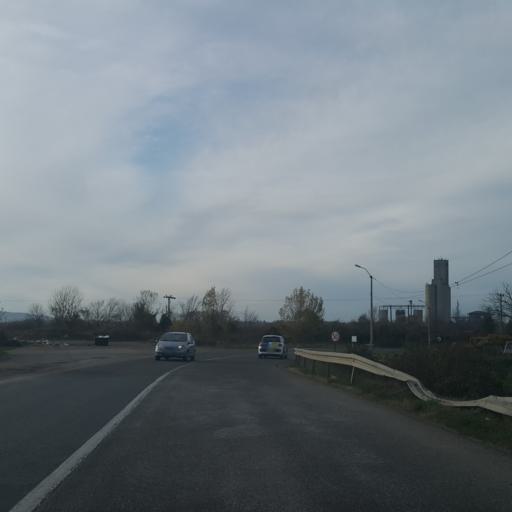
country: RS
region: Central Serbia
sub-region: Kolubarski Okrug
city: Lajkovac
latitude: 44.3674
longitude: 20.1934
